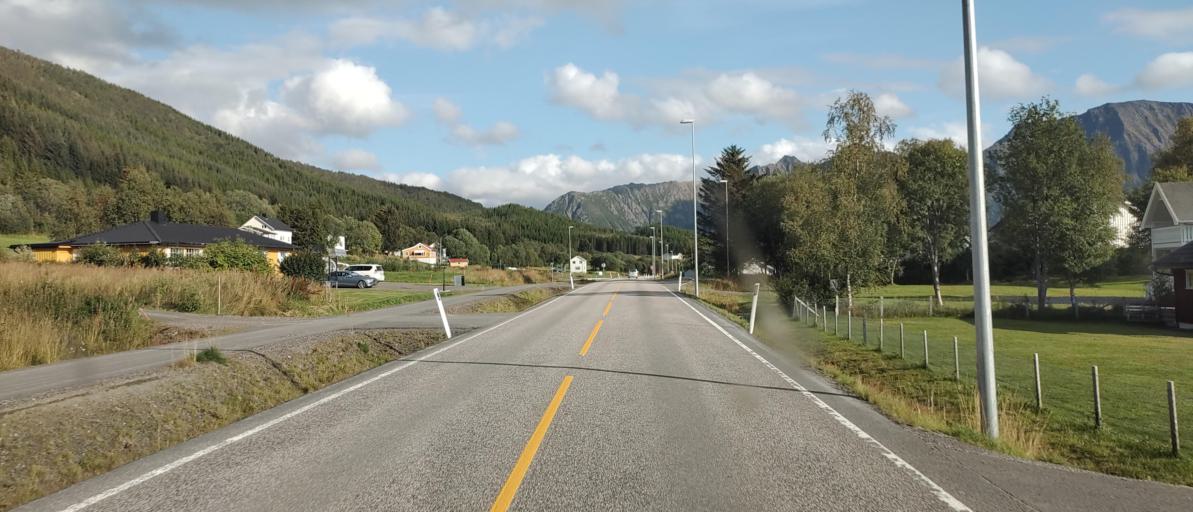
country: NO
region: Nordland
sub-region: Sortland
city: Sortland
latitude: 68.7502
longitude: 15.4924
